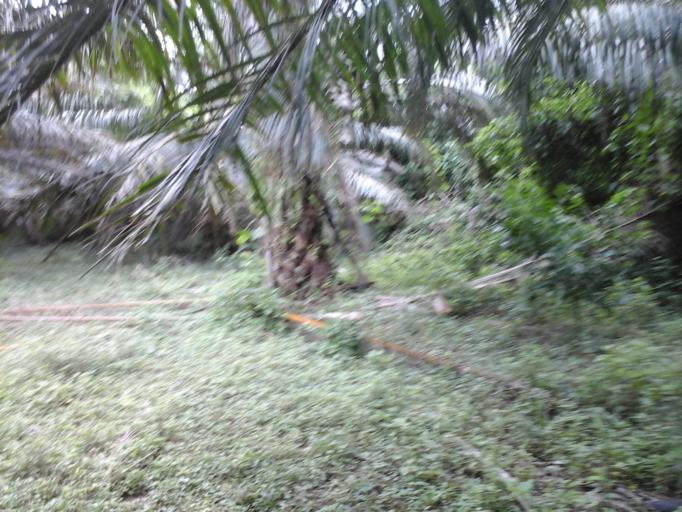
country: CO
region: Bolivar
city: San Pablo
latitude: 10.1594
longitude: -75.2747
